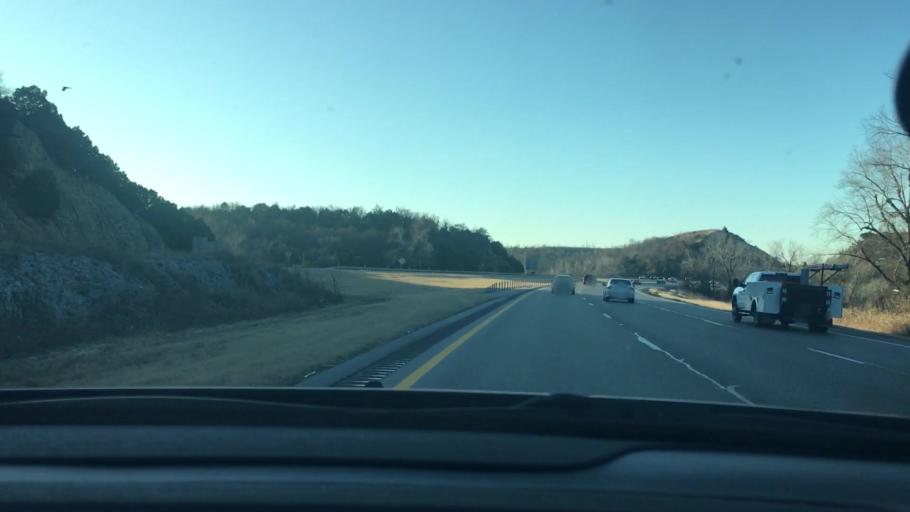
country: US
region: Oklahoma
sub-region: Murray County
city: Davis
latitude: 34.4404
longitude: -97.1287
